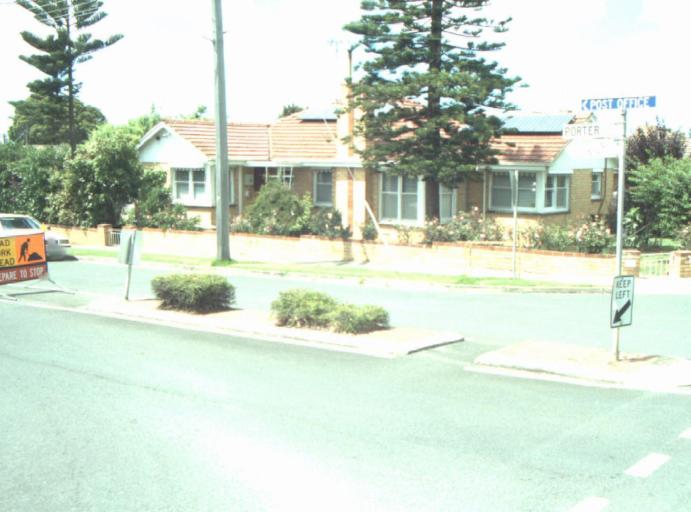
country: AU
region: Victoria
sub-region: Greater Geelong
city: Wandana Heights
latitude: -38.1809
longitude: 144.3169
